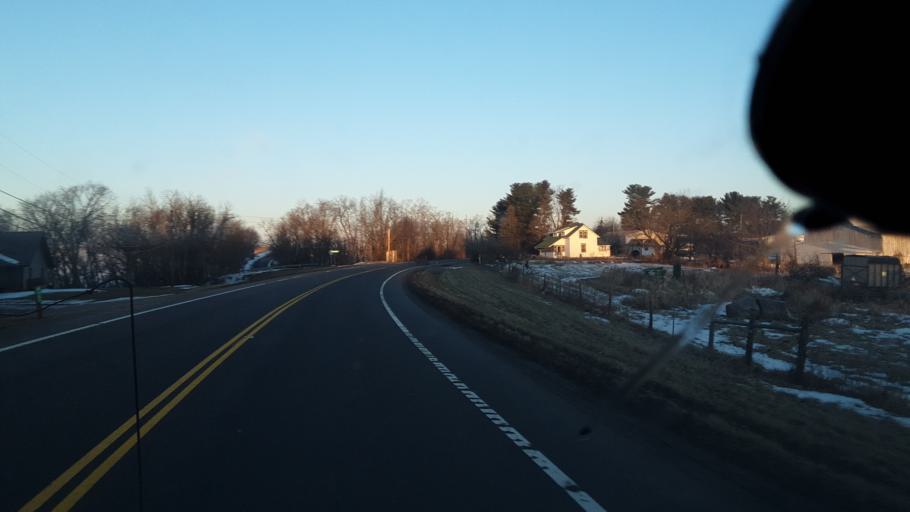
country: US
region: Ohio
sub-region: Perry County
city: Somerset
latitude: 39.8138
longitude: -82.3138
